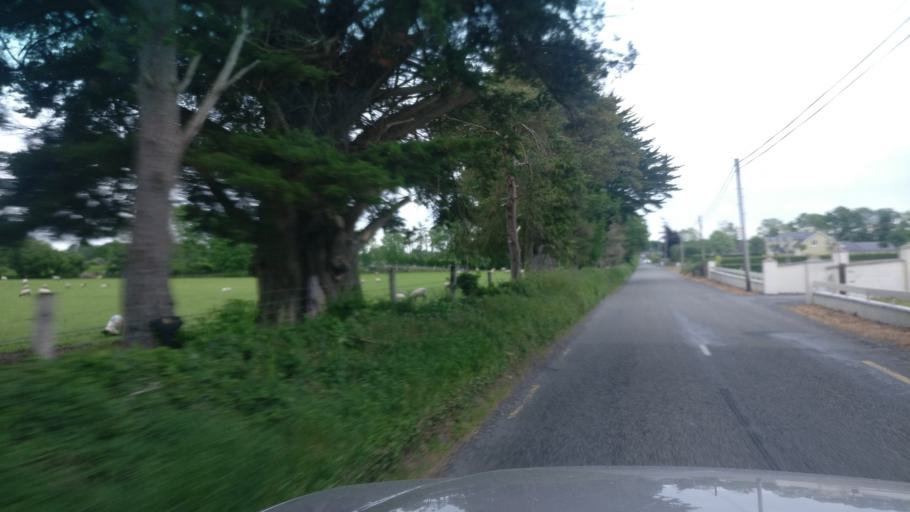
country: IE
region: Connaught
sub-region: County Galway
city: Portumna
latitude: 53.0968
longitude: -8.2439
